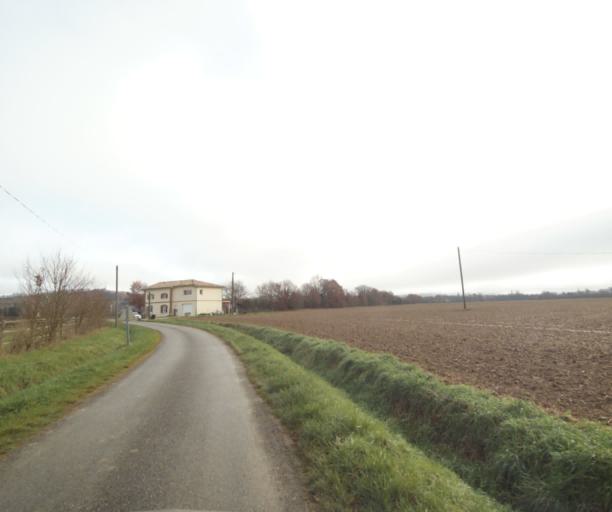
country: FR
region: Midi-Pyrenees
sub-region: Departement de la Haute-Garonne
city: Villemur-sur-Tarn
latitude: 43.8742
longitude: 1.4812
